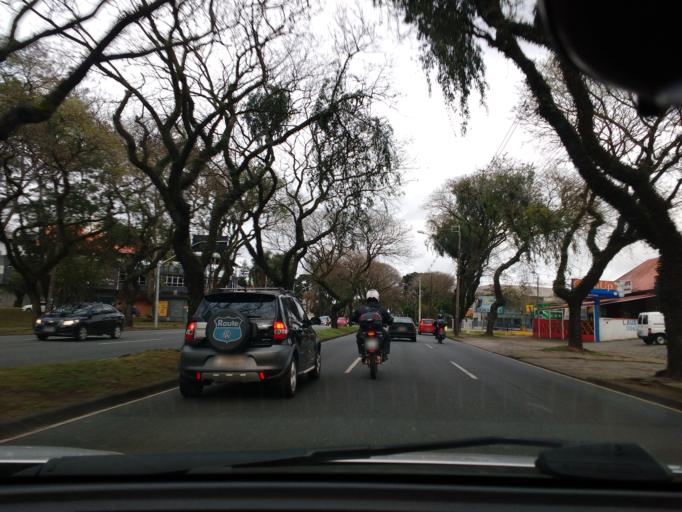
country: BR
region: Parana
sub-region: Curitiba
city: Curitiba
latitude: -25.4279
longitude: -49.2339
